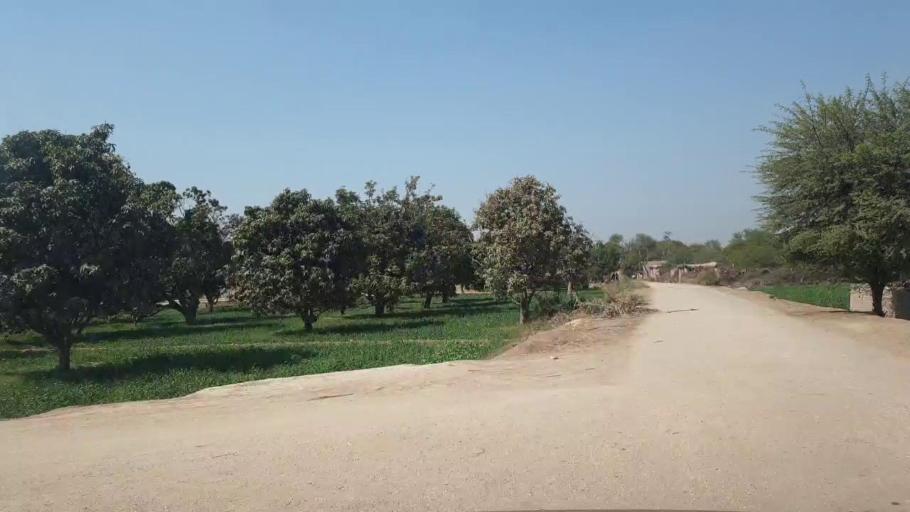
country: PK
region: Sindh
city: Tando Jam
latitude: 25.3278
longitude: 68.6332
